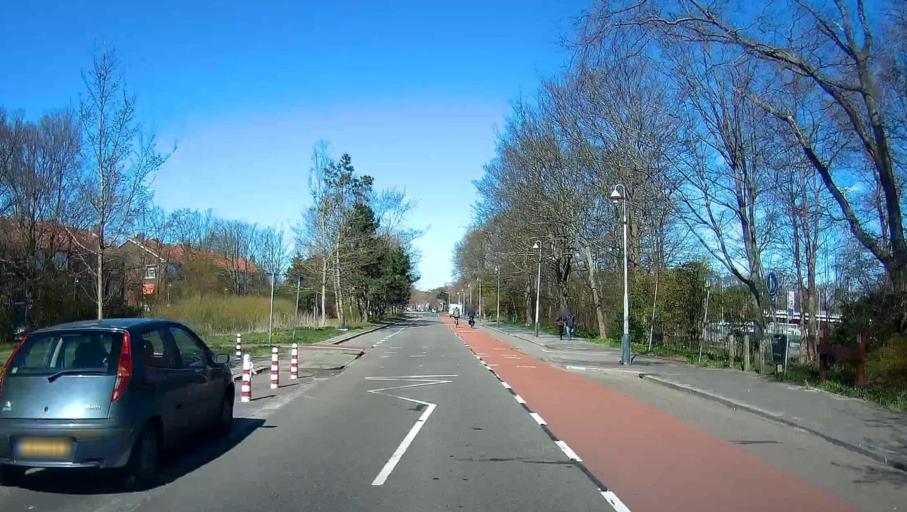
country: NL
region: South Holland
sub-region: Gemeente Den Haag
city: Scheveningen
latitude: 52.0705
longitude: 4.2427
